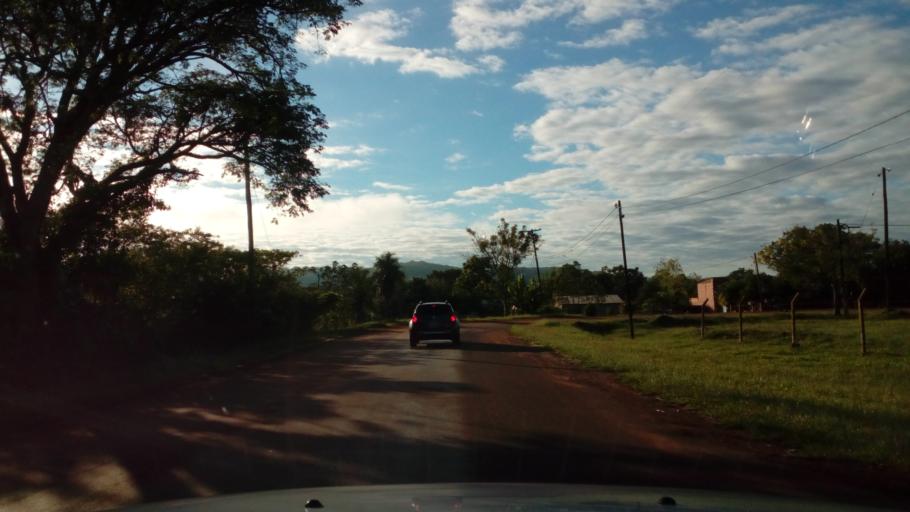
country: AR
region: Misiones
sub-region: Departamento de San Javier
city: San Javier
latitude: -27.8867
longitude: -55.1325
